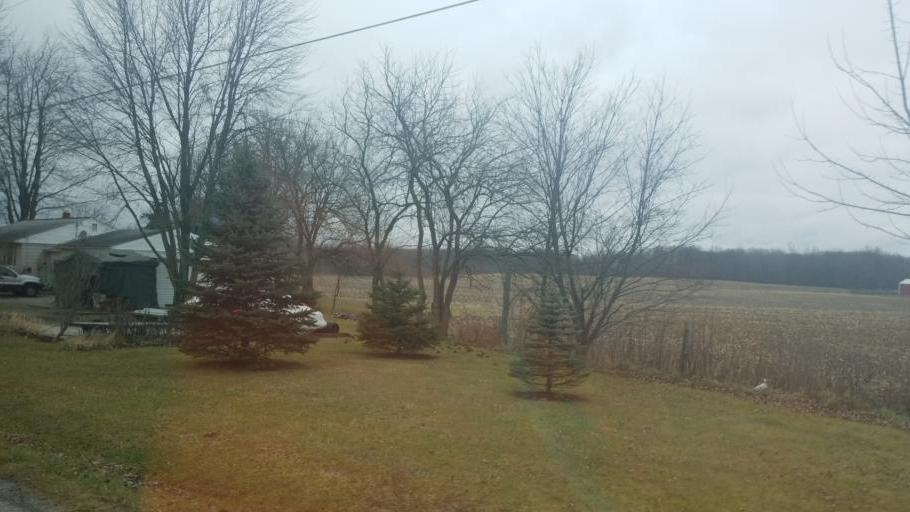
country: US
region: Ohio
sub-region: Crawford County
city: Galion
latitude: 40.7500
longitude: -82.7557
